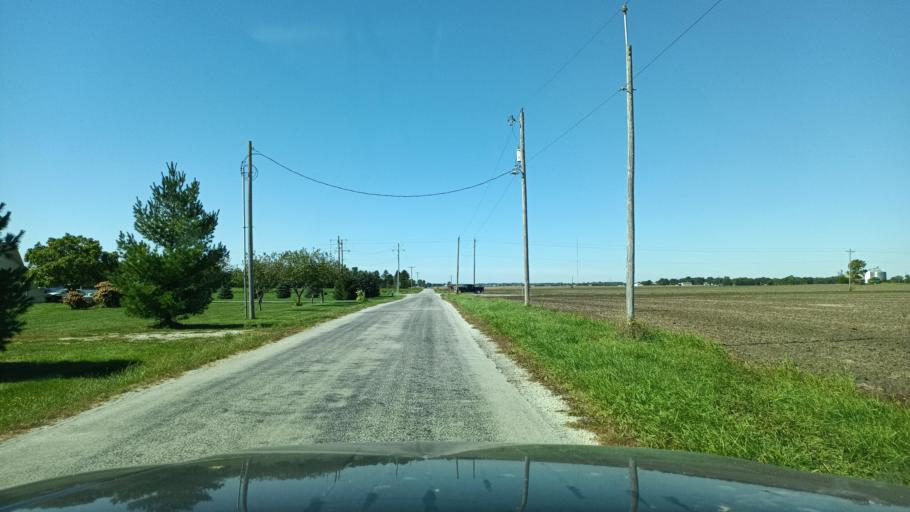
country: US
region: Illinois
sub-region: Champaign County
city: Mahomet
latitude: 40.0987
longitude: -88.4058
